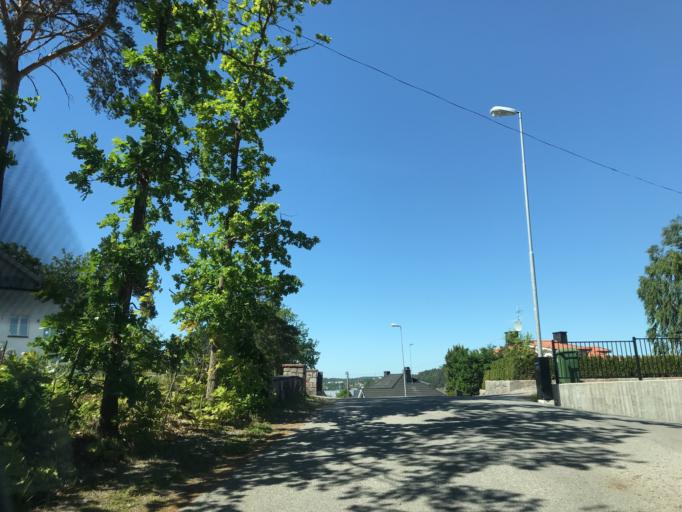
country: SE
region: Stockholm
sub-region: Sollentuna Kommun
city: Sollentuna
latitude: 59.4215
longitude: 17.9798
